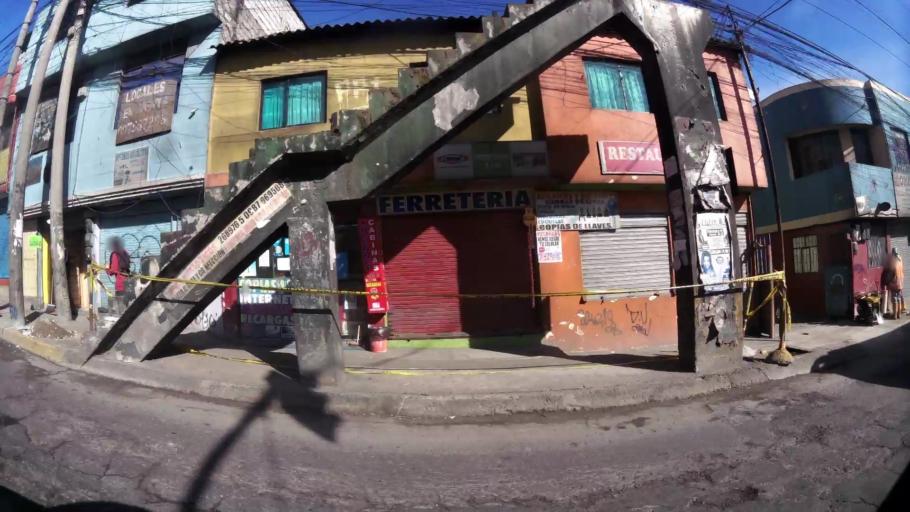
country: EC
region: Pichincha
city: Quito
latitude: -0.3175
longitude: -78.5492
